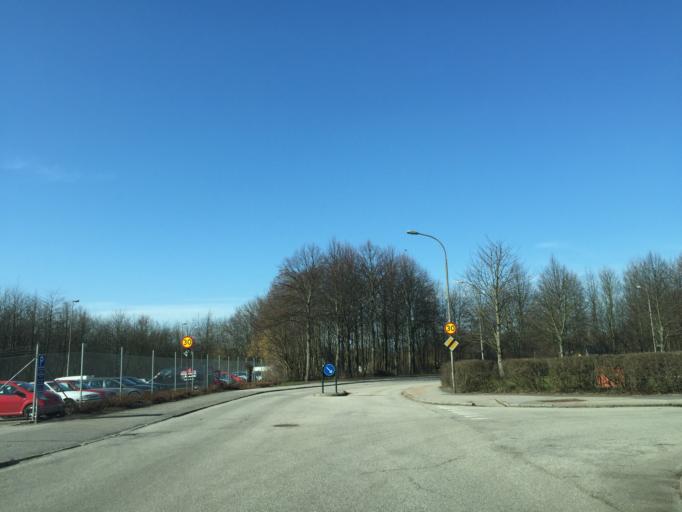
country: SE
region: Skane
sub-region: Lunds Kommun
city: Lund
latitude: 55.6910
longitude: 13.1718
